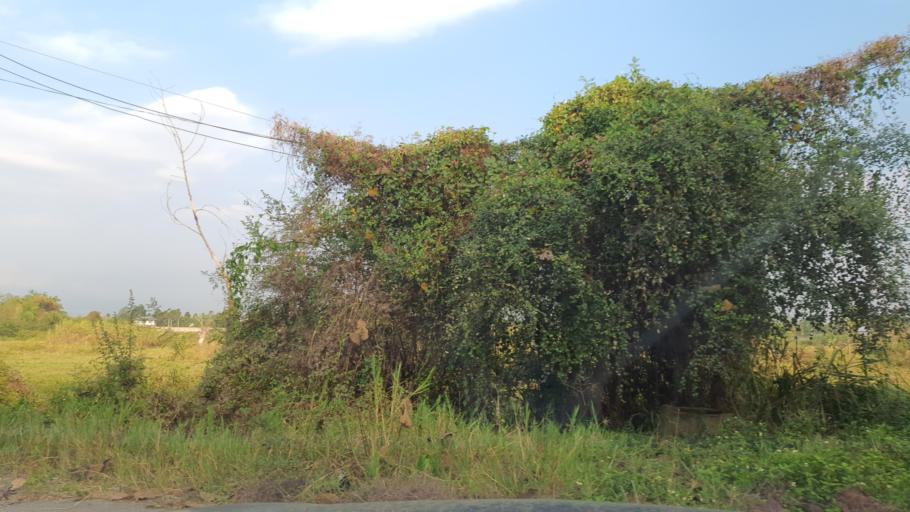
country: TH
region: Chiang Mai
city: San Kamphaeng
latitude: 18.7318
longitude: 99.1024
